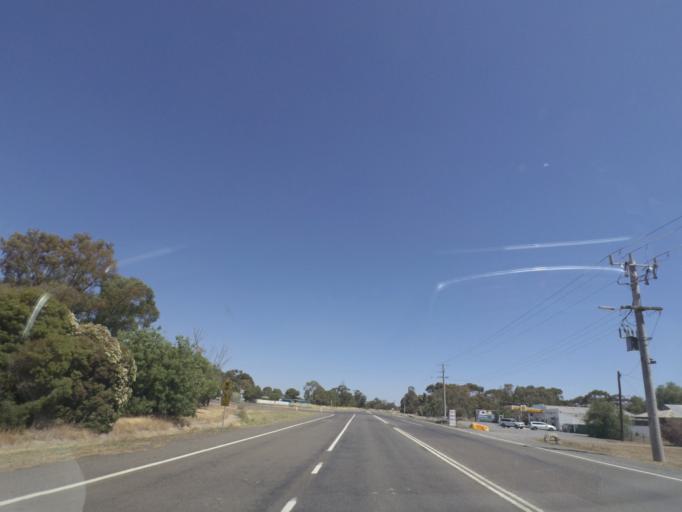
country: AU
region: Victoria
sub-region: Greater Shepparton
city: Shepparton
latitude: -36.2381
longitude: 145.4315
